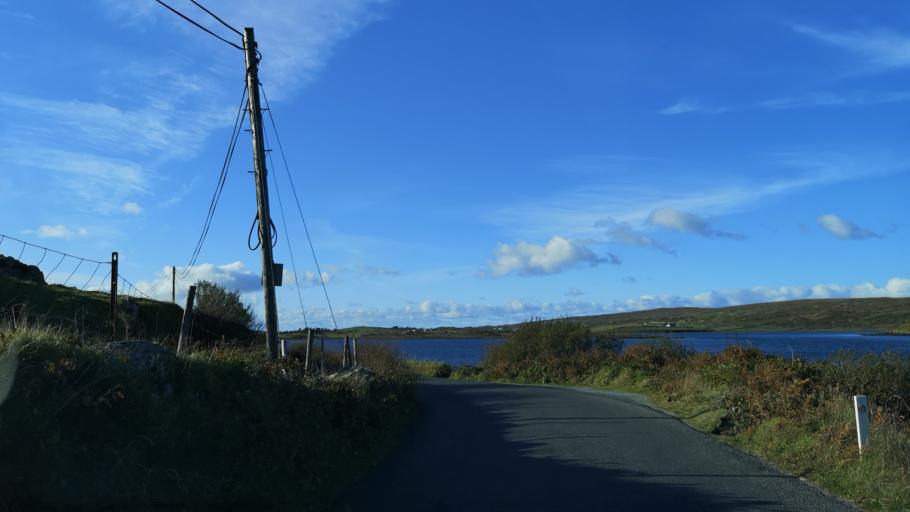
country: IE
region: Connaught
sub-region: County Galway
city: Clifden
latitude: 53.5040
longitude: -10.0644
